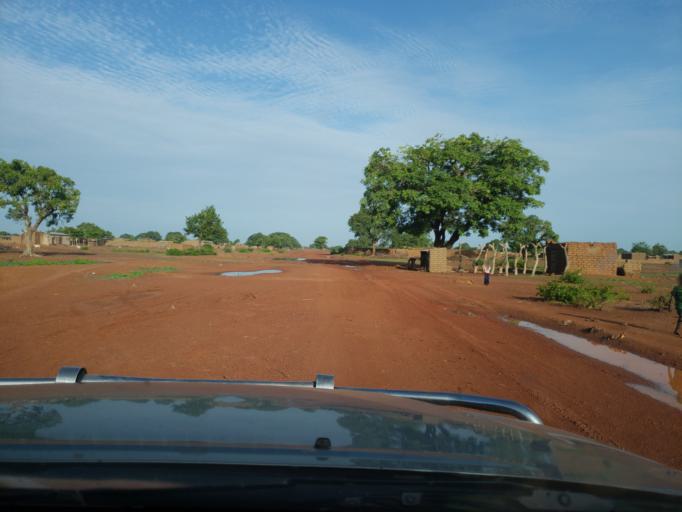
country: ML
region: Sikasso
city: Koutiala
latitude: 12.4292
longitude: -5.6156
